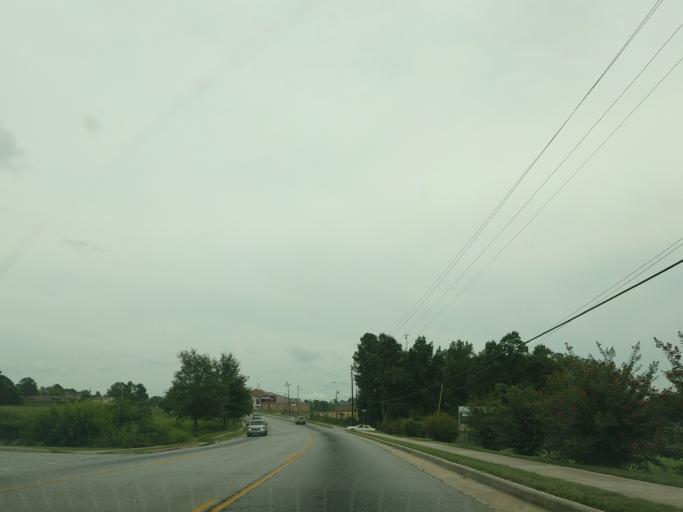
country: US
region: Georgia
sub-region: Bibb County
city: Macon
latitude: 32.8208
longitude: -83.6767
